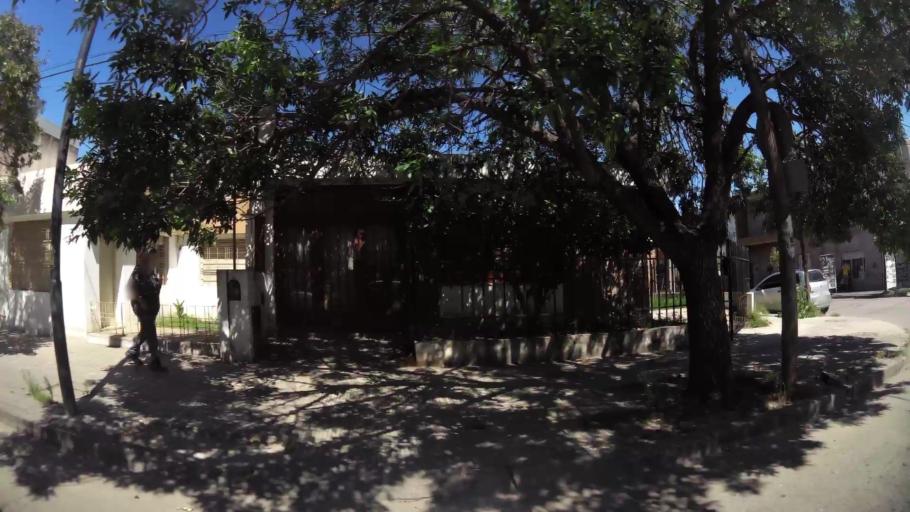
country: AR
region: Cordoba
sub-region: Departamento de Capital
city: Cordoba
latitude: -31.4199
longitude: -64.1400
